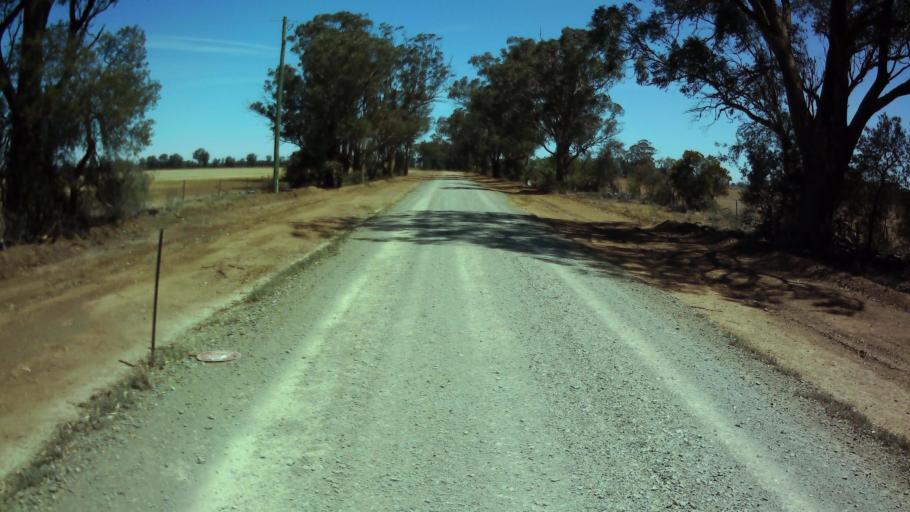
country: AU
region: New South Wales
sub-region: Weddin
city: Grenfell
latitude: -33.9097
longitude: 147.6848
